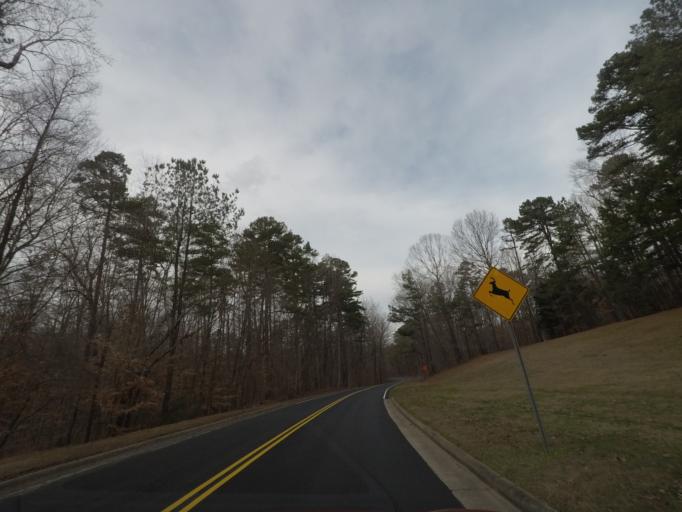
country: US
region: North Carolina
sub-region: Durham County
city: Durham
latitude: 36.0398
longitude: -78.9518
